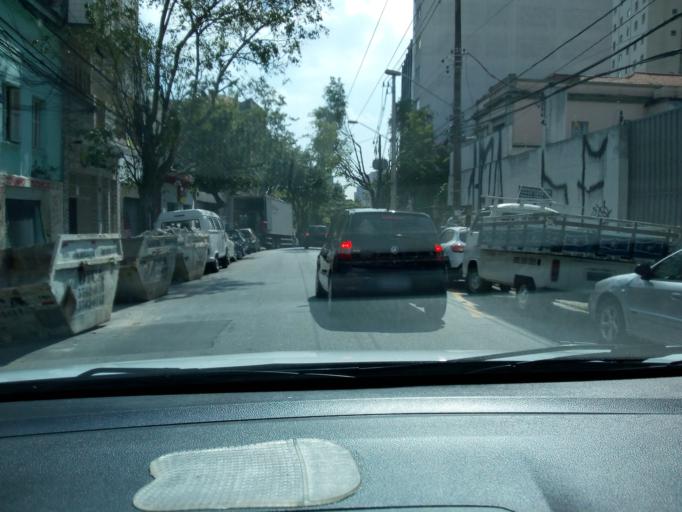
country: BR
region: Sao Paulo
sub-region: Sao Paulo
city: Sao Paulo
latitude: -23.5628
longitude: -46.6316
